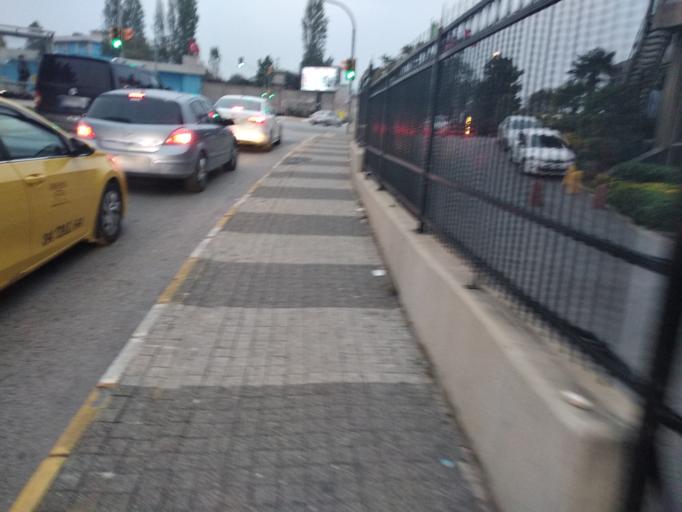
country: TR
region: Istanbul
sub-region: Atasehir
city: Atasehir
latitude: 40.9829
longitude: 29.1338
